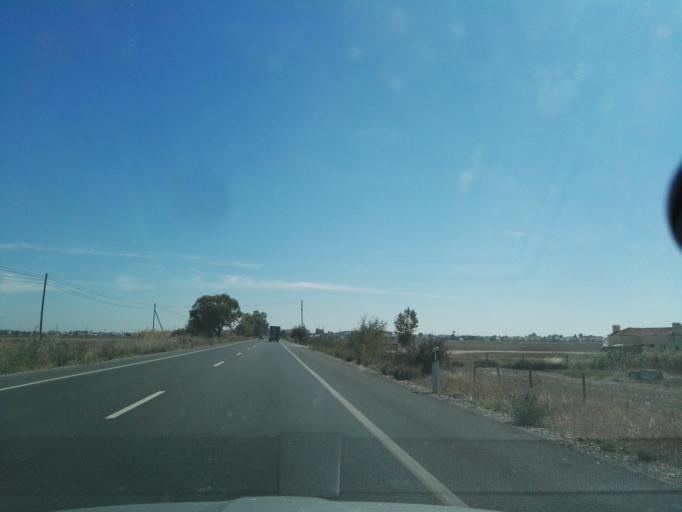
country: PT
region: Santarem
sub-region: Benavente
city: Samora Correia
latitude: 38.9288
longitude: -8.9041
